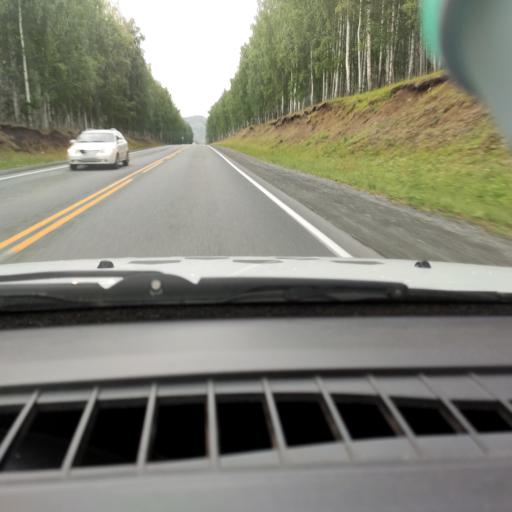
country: RU
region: Chelyabinsk
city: Karabash
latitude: 55.3301
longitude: 60.2318
